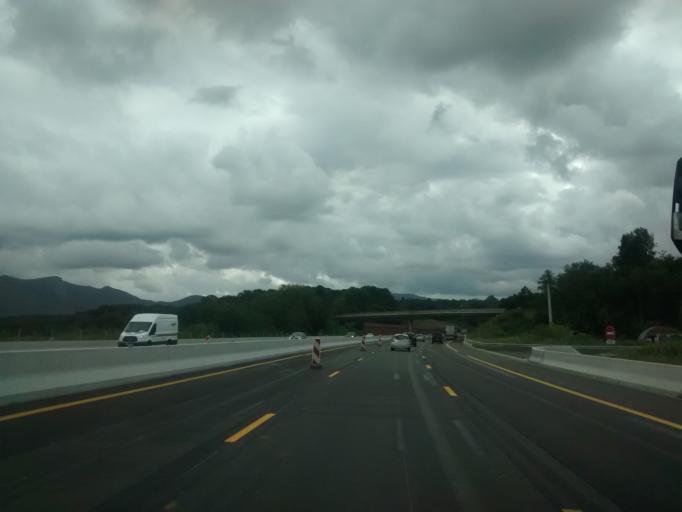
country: FR
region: Aquitaine
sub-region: Departement des Pyrenees-Atlantiques
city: Saint-Jean-de-Luz
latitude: 43.3788
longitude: -1.6460
